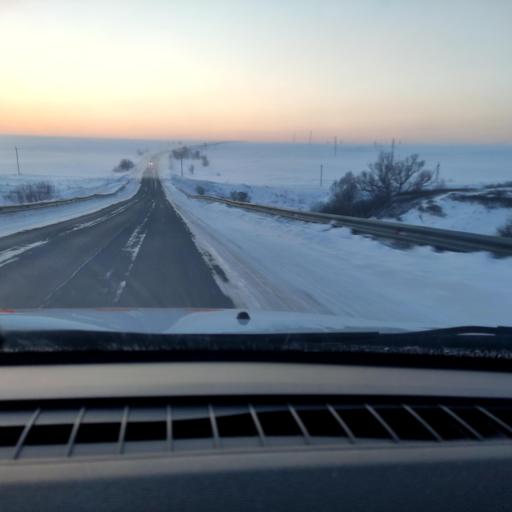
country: RU
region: Samara
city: Georgiyevka
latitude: 53.4164
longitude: 50.8799
